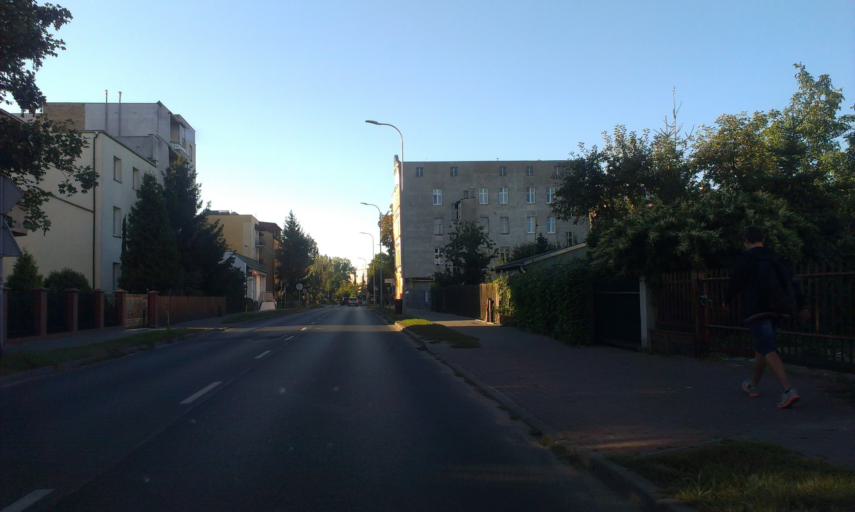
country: PL
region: Kujawsko-Pomorskie
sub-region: Torun
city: Torun
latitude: 53.0220
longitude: 18.6018
